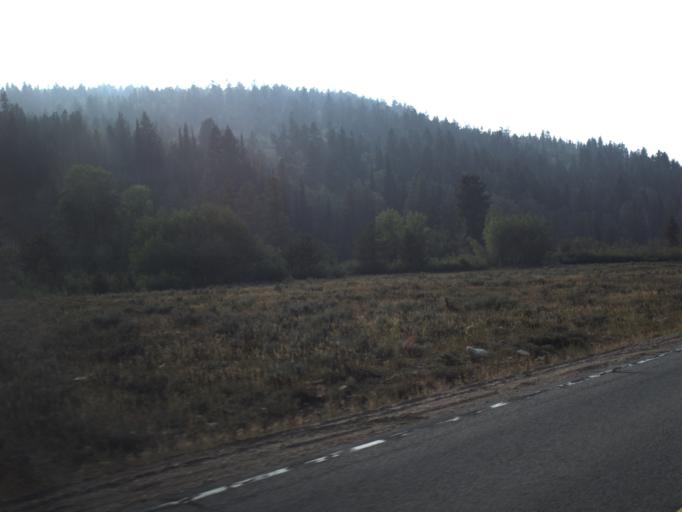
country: US
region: Utah
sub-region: Summit County
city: Francis
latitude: 40.6122
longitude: -111.1261
